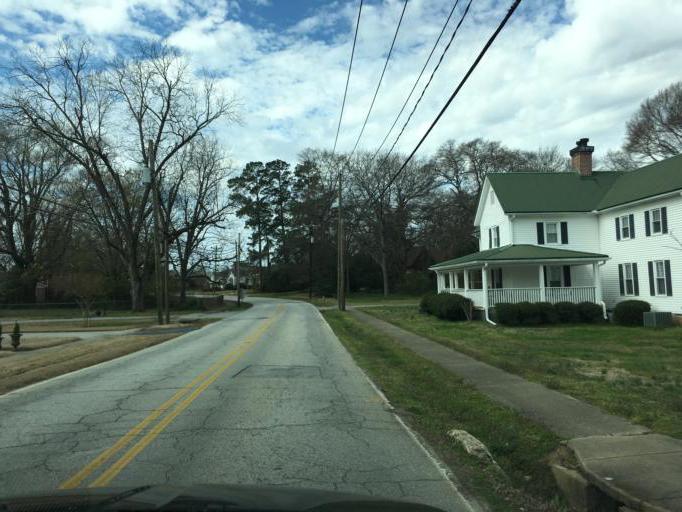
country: US
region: South Carolina
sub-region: Greenville County
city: Fountain Inn
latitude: 34.6936
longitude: -82.1952
